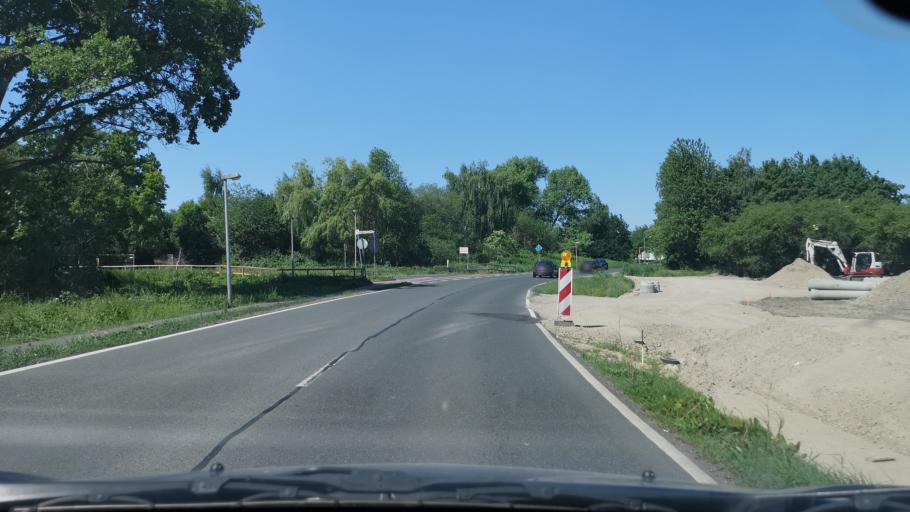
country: DE
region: Lower Saxony
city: Garbsen-Mitte
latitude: 52.4263
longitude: 9.6098
